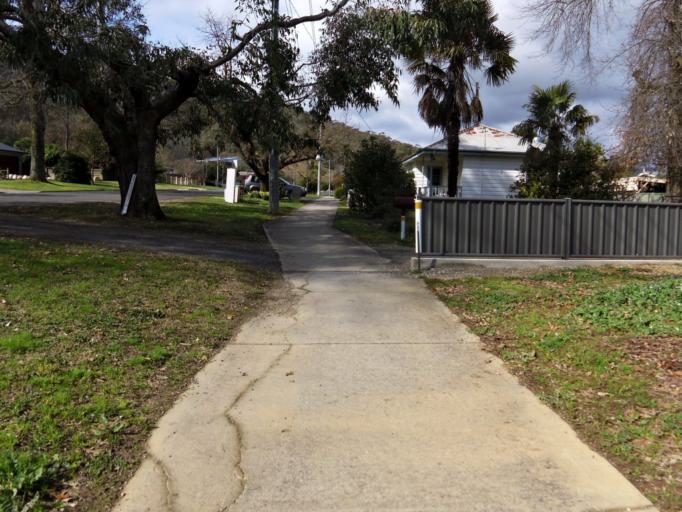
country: AU
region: Victoria
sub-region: Wangaratta
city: Wangaratta
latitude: -36.5635
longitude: 146.7294
